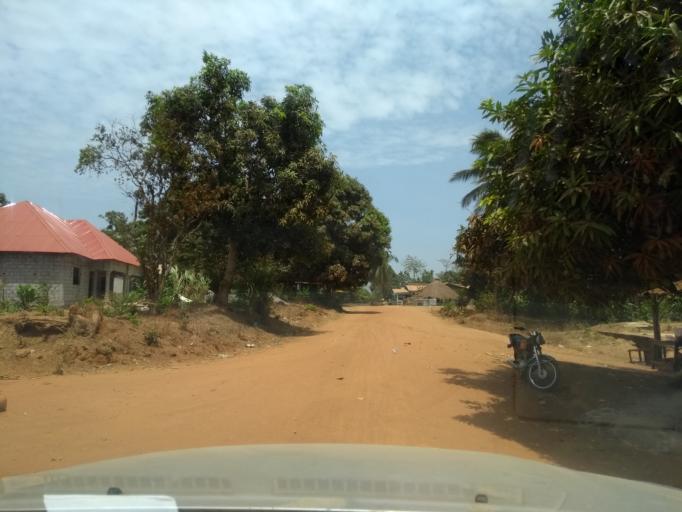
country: GN
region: Kindia
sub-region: Prefecture de Dubreka
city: Dubreka
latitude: 9.7863
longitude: -13.5432
